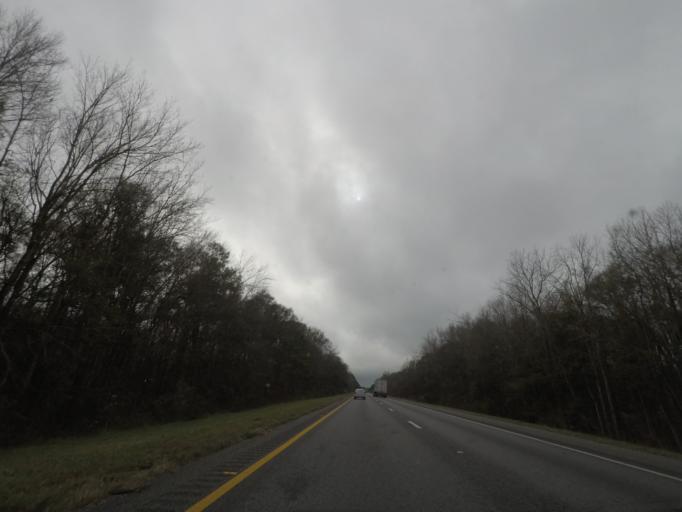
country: US
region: South Carolina
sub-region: Orangeburg County
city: Holly Hill
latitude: 33.3418
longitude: -80.5351
